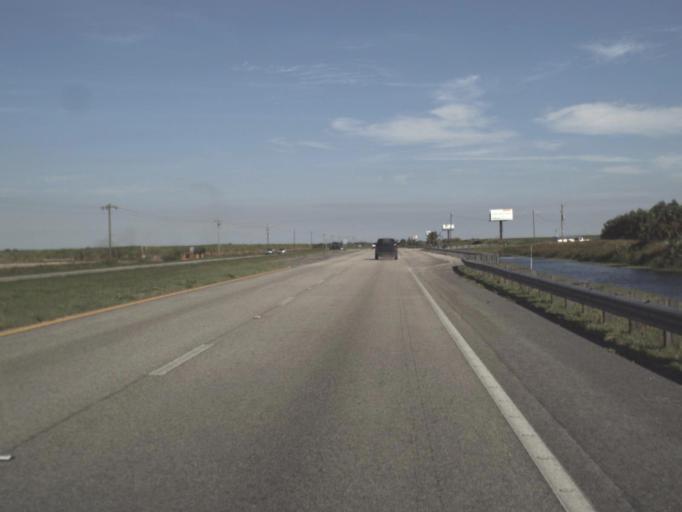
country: US
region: Florida
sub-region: Glades County
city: Moore Haven
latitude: 26.7535
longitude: -81.0668
